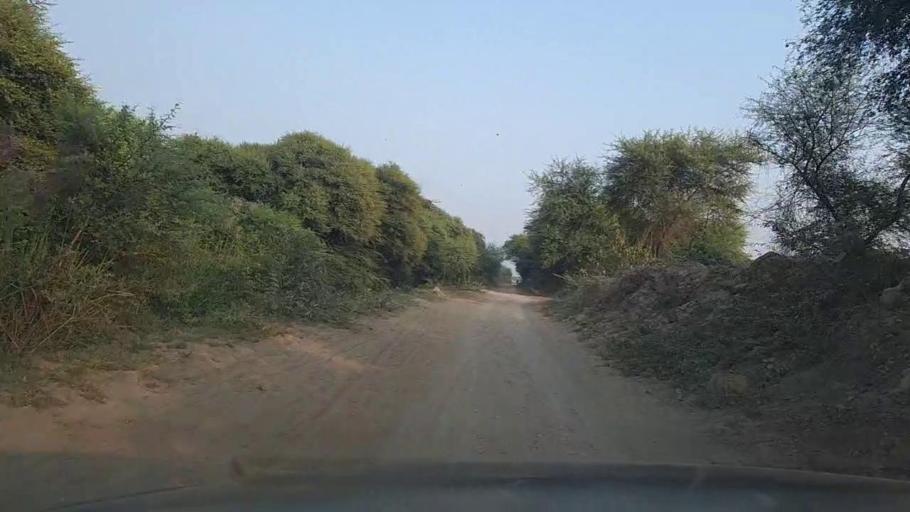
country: PK
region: Sindh
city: Mirpur Batoro
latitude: 24.5475
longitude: 68.3474
